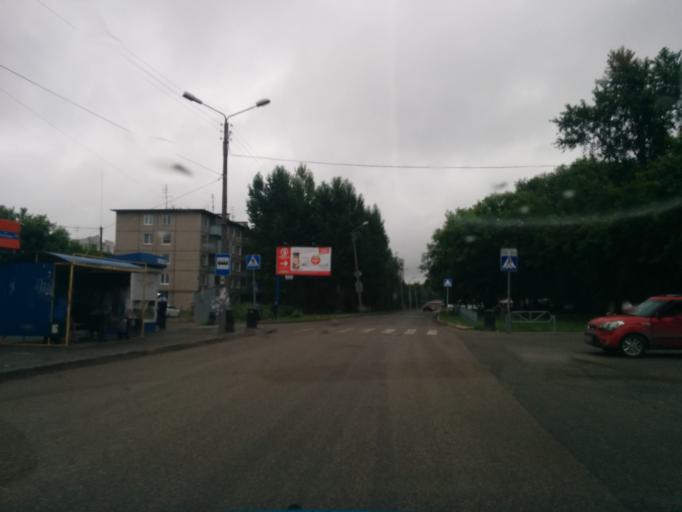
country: RU
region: Perm
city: Perm
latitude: 57.9927
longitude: 56.2304
